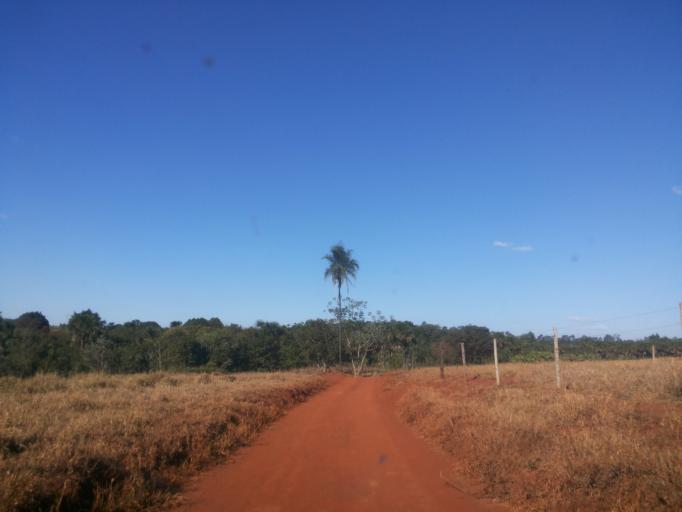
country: BR
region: Minas Gerais
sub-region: Centralina
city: Centralina
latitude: -18.7401
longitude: -49.1611
